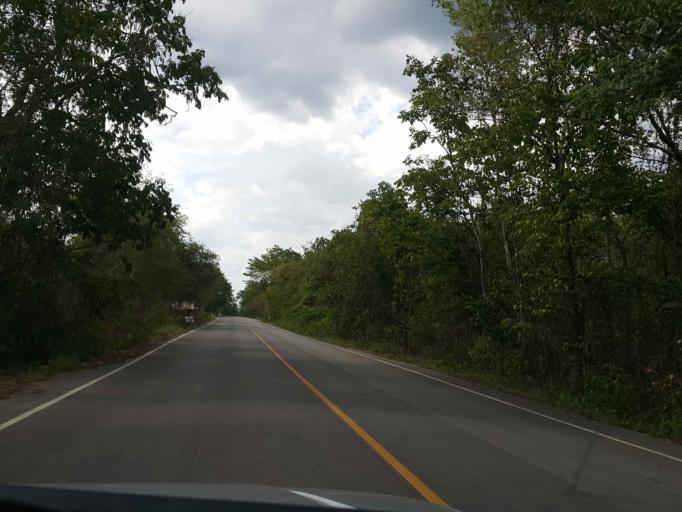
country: TH
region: Sukhothai
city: Thung Saliam
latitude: 17.3856
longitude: 99.3987
